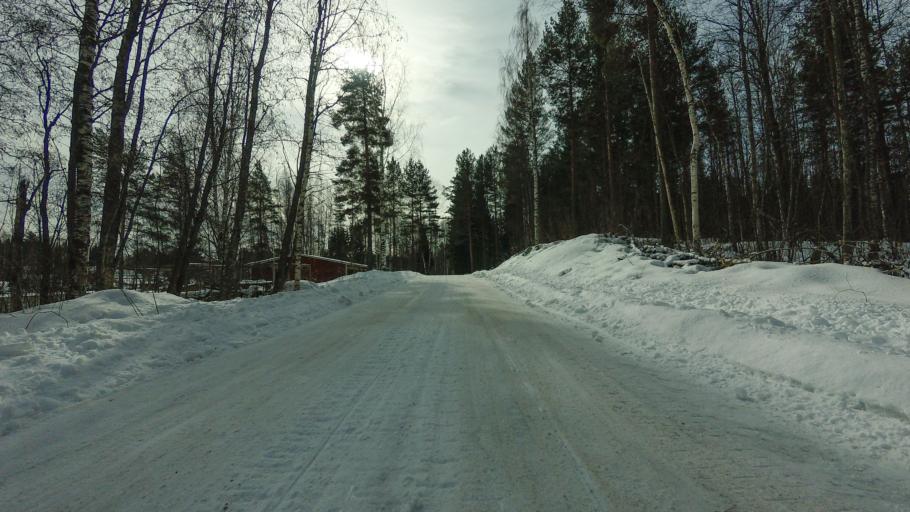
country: FI
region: Southern Savonia
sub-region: Savonlinna
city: Rantasalmi
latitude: 62.1180
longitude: 28.6045
